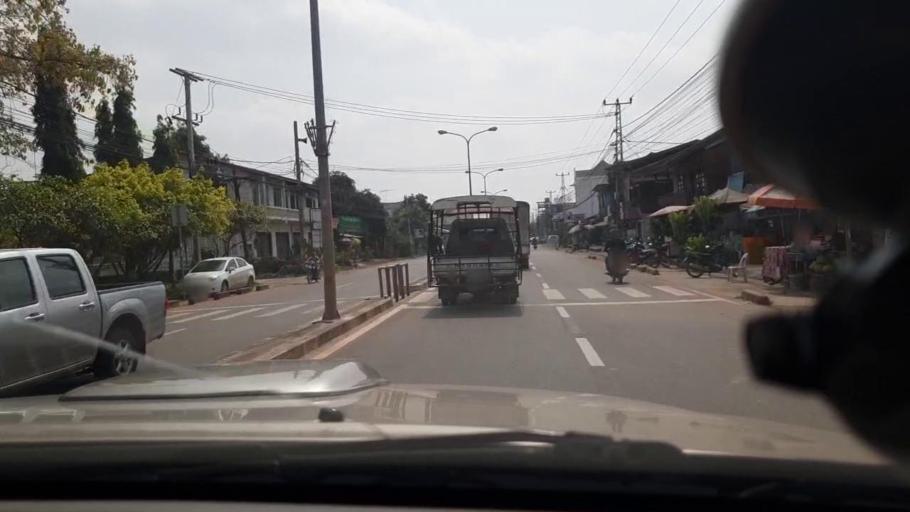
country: TH
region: Nong Khai
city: Si Chiang Mai
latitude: 17.9227
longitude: 102.6177
